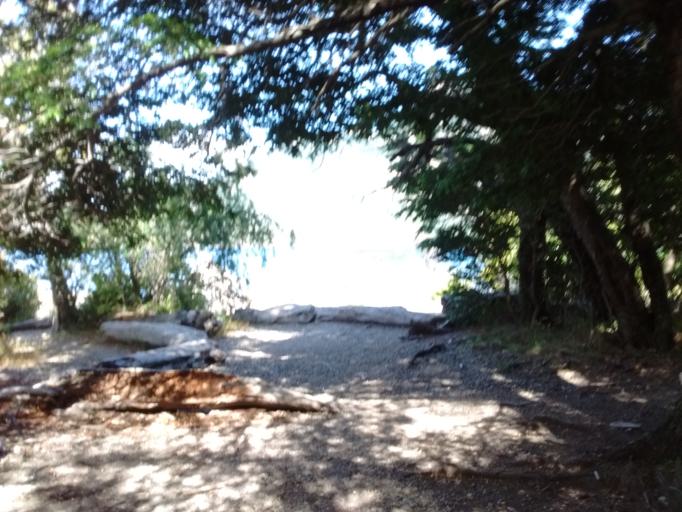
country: AR
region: Rio Negro
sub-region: Departamento de Bariloche
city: San Carlos de Bariloche
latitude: -41.0634
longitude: -71.5699
